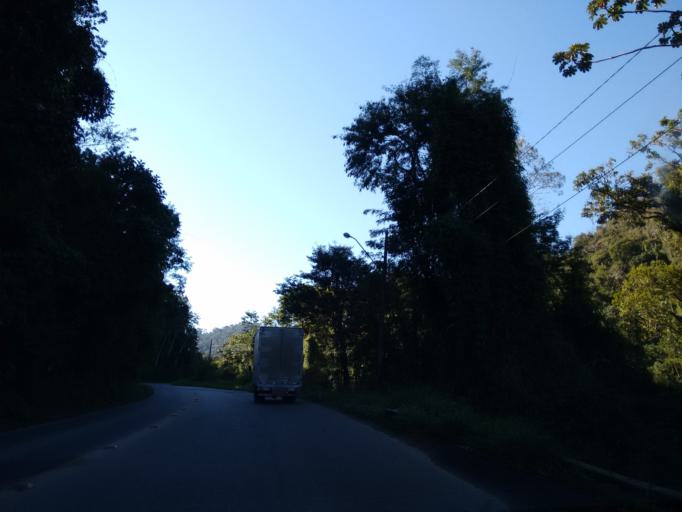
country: BR
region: Santa Catarina
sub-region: Pomerode
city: Pomerode
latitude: -26.6542
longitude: -49.1404
